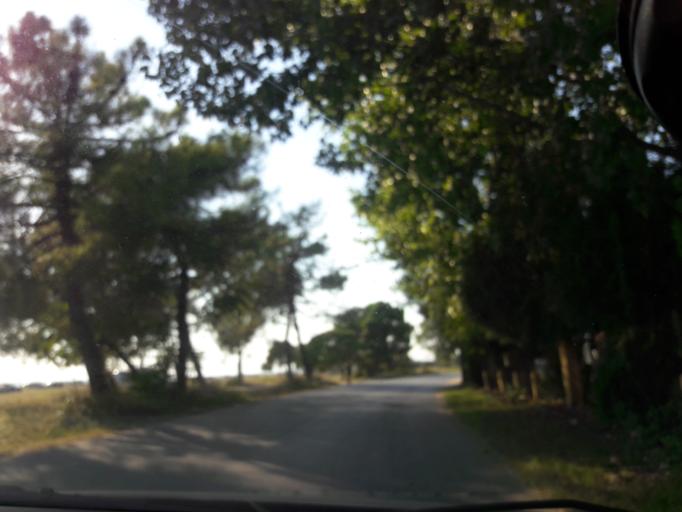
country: GR
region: Central Macedonia
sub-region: Nomos Chalkidikis
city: Nea Kallikrateia
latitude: 40.3360
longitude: 23.0210
